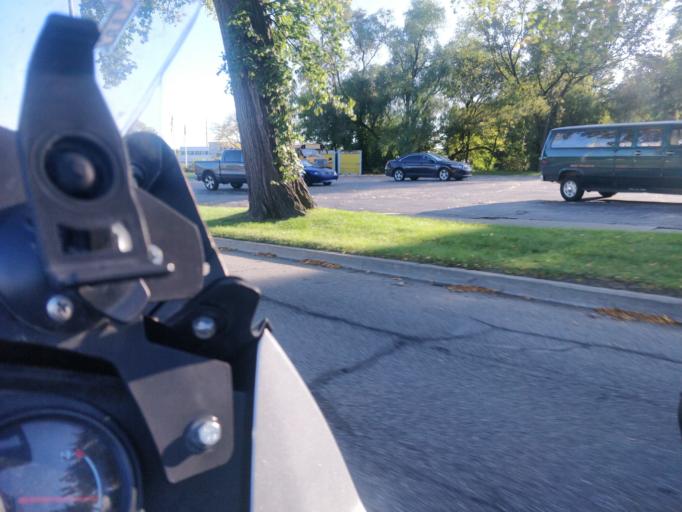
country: US
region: Michigan
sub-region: Wayne County
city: Melvindale
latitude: 42.2676
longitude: -83.1779
